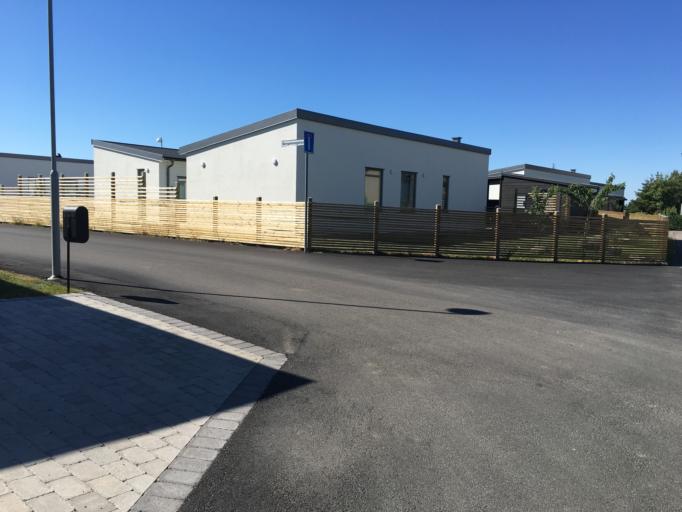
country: SE
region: Skane
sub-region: Hoganas Kommun
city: Hoganas
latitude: 56.1502
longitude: 12.5888
